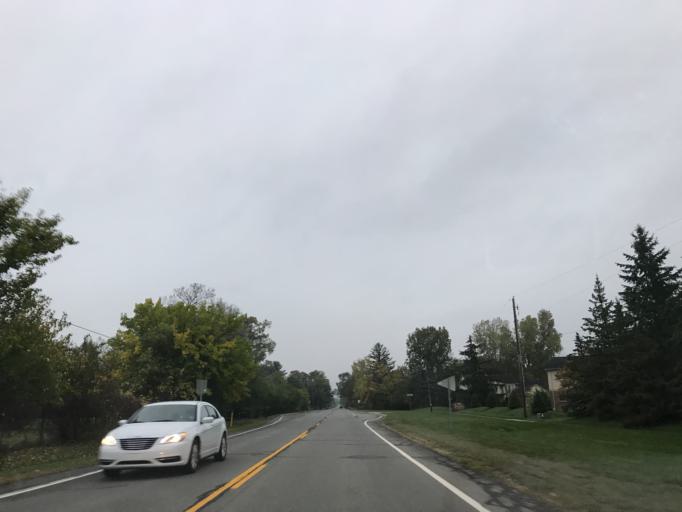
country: US
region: Michigan
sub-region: Oakland County
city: Franklin
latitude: 42.4669
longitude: -83.3181
